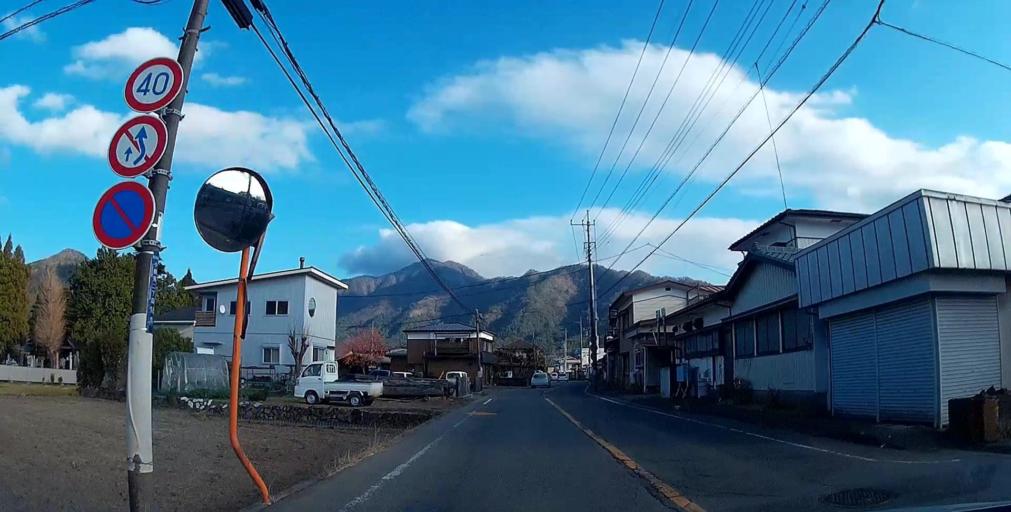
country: JP
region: Yamanashi
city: Fujikawaguchiko
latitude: 35.4950
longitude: 138.8223
